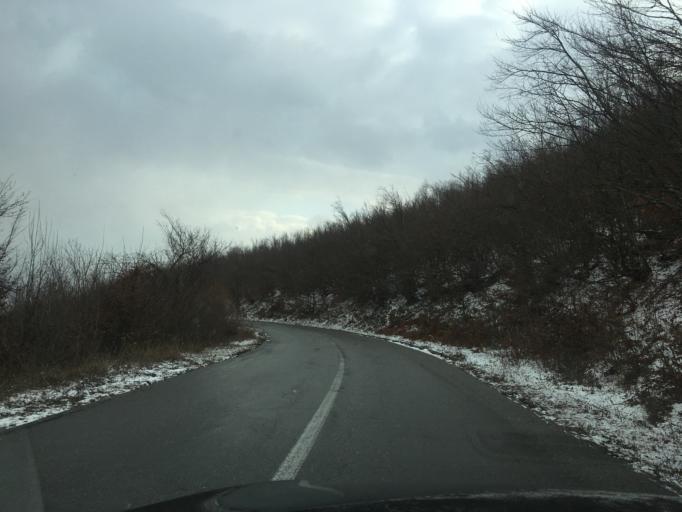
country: XK
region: Pec
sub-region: Komuna e Pejes
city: Dubova (Driloni)
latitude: 42.7518
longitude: 20.3017
